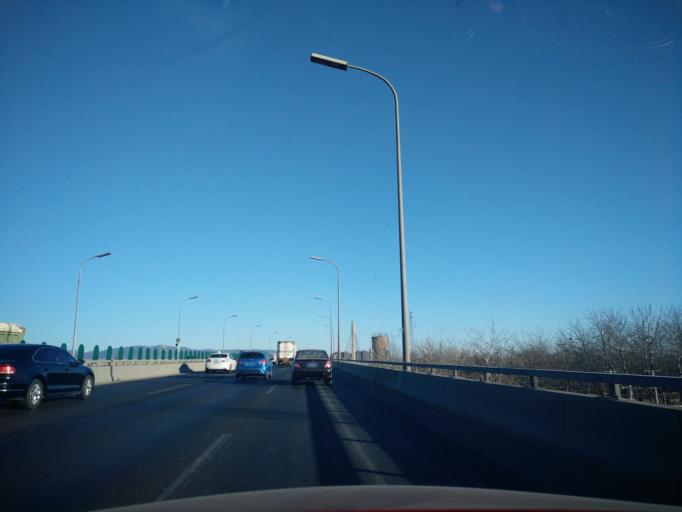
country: CN
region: Beijing
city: Lugu
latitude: 39.8750
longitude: 116.2021
